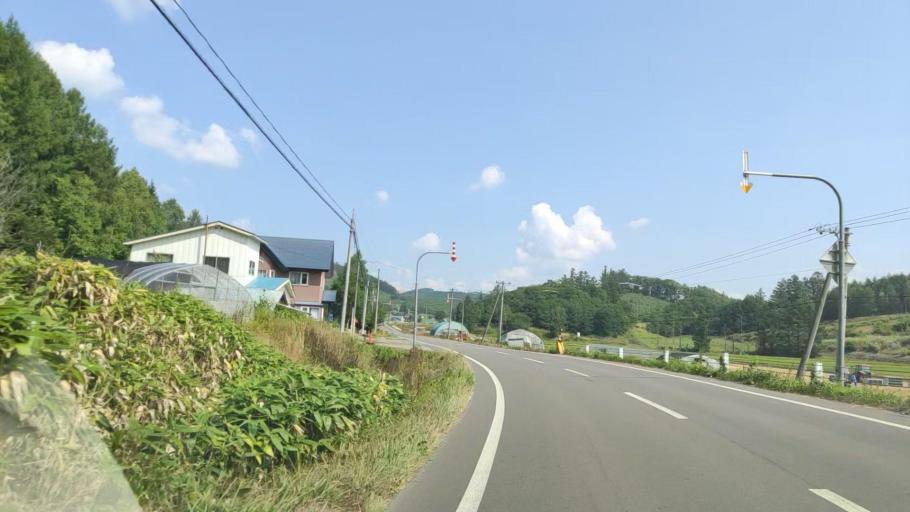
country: JP
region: Hokkaido
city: Shimo-furano
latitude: 43.4316
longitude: 142.4095
